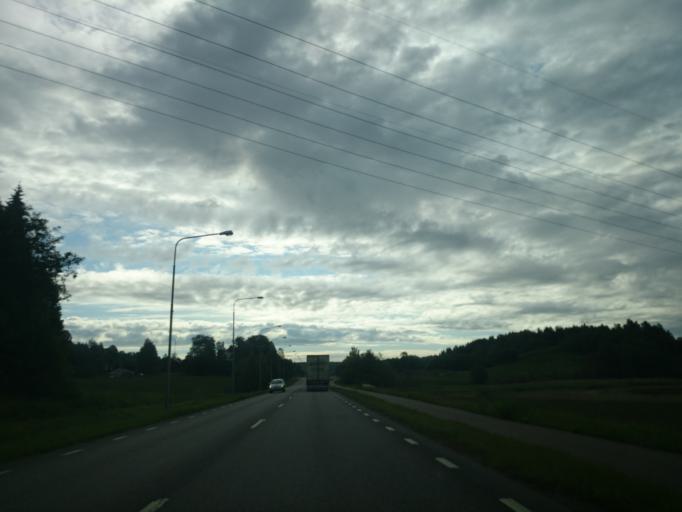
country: SE
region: Vaesternorrland
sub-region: Sundsvalls Kommun
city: Johannedal
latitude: 62.4133
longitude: 17.3613
